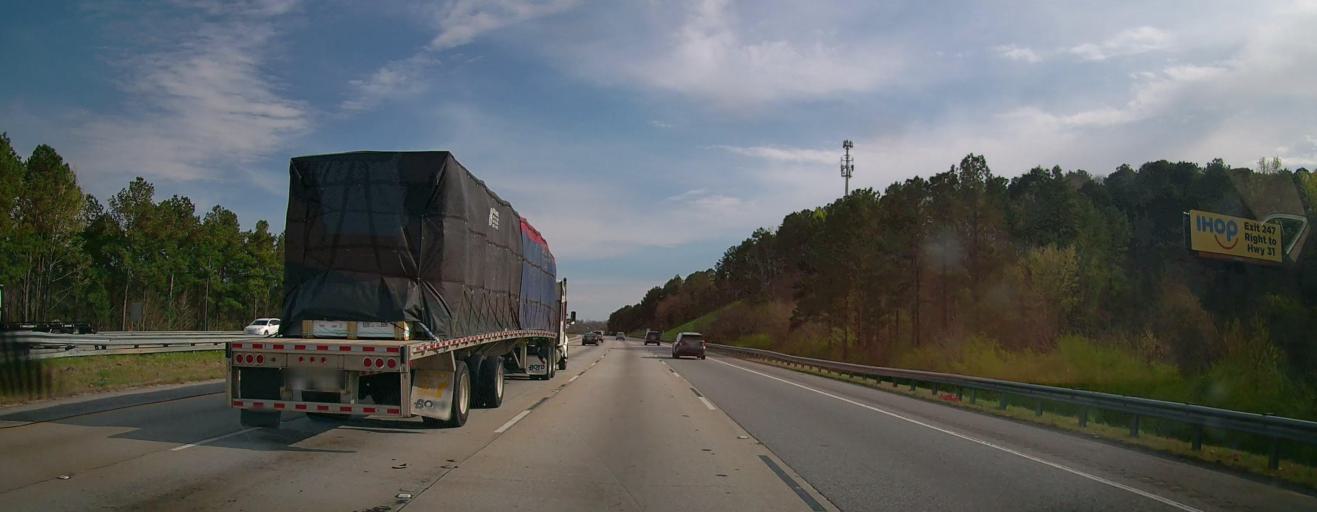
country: US
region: Alabama
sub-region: Shelby County
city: Indian Springs Village
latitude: 33.3800
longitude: -86.7818
